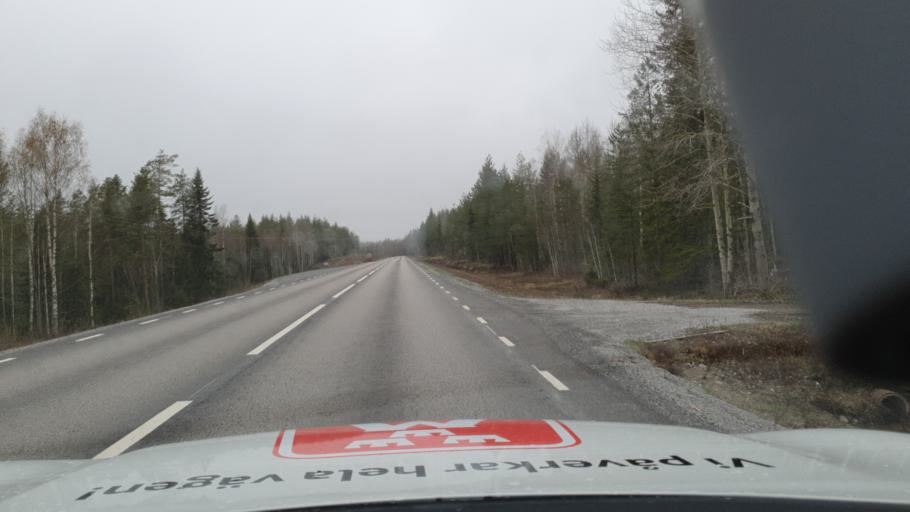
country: SE
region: Vaesterbotten
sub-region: Umea Kommun
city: Hoernefors
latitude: 63.7727
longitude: 19.9686
